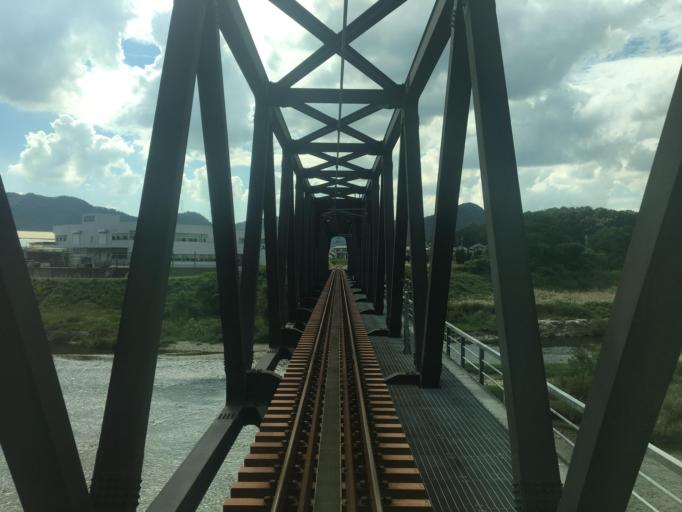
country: JP
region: Hyogo
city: Nishiwaki
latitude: 34.9767
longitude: 134.9740
